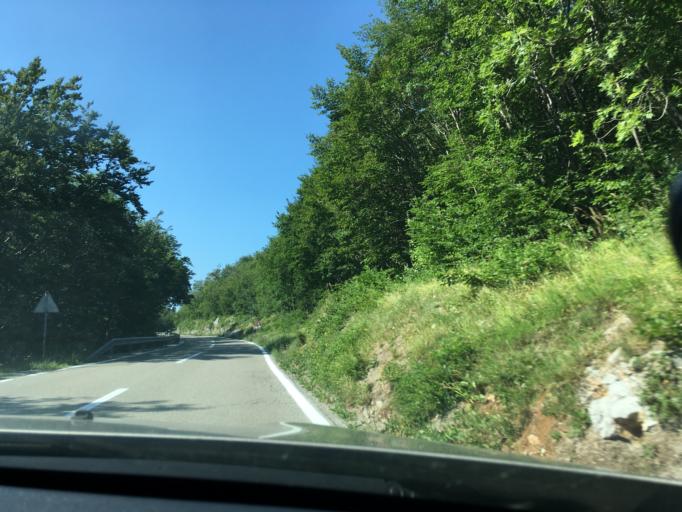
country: HR
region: Primorsko-Goranska
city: Hreljin
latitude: 45.3462
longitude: 14.6111
